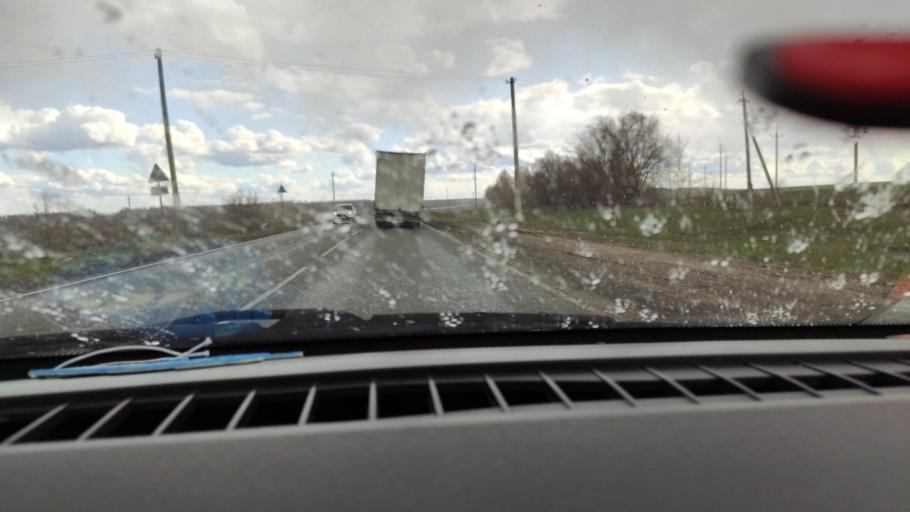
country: RU
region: Saratov
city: Balakovo
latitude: 52.1132
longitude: 47.7499
